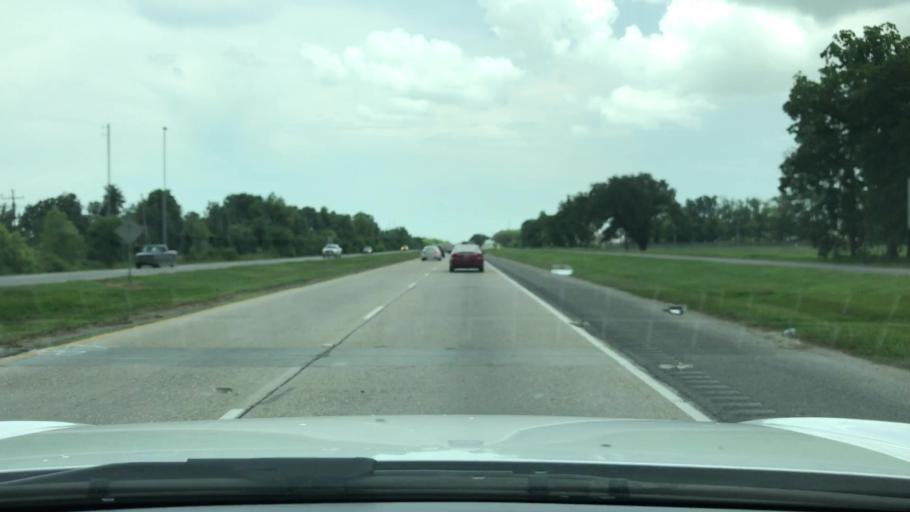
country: US
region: Louisiana
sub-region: Iberville Parish
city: Plaquemine
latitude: 30.3156
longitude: -91.2494
